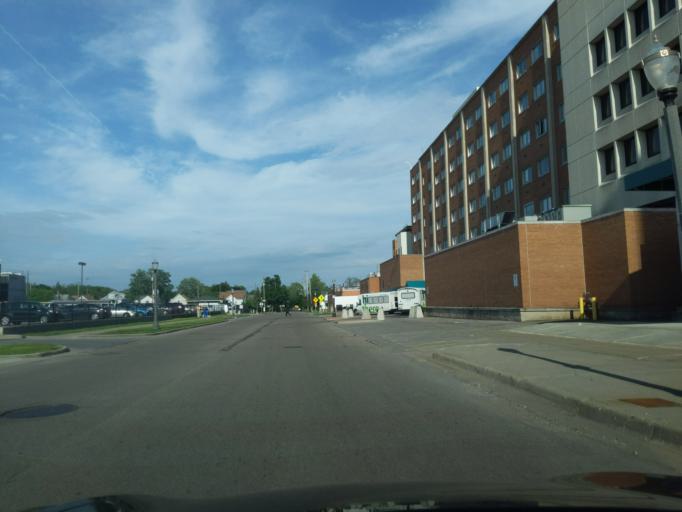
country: US
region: Michigan
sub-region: Ingham County
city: Lansing
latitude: 42.7347
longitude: -84.5353
